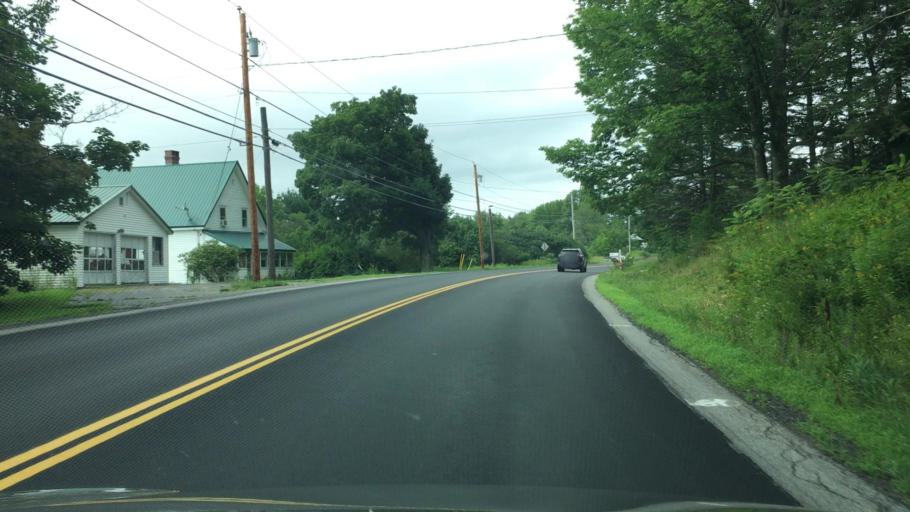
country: US
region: Maine
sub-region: Waldo County
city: Winterport
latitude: 44.6203
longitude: -68.8312
